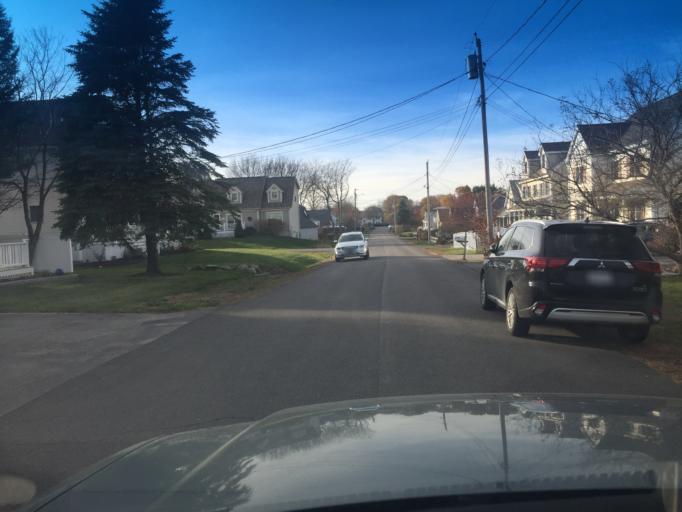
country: US
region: Maine
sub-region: York County
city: York Beach
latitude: 43.1706
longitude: -70.6034
